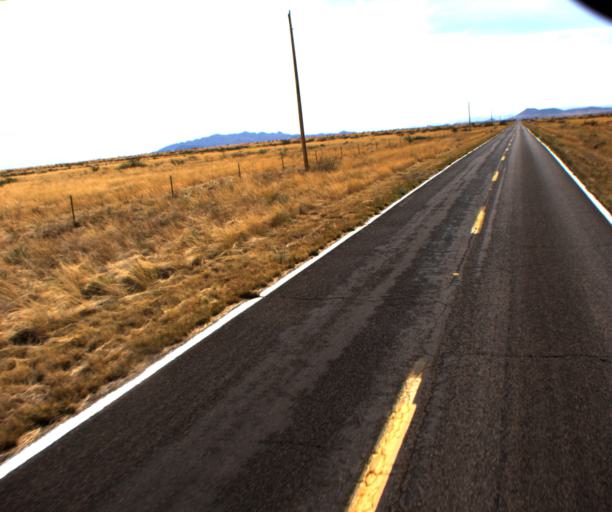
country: US
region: Arizona
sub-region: Cochise County
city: Willcox
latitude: 31.9449
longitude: -109.4823
